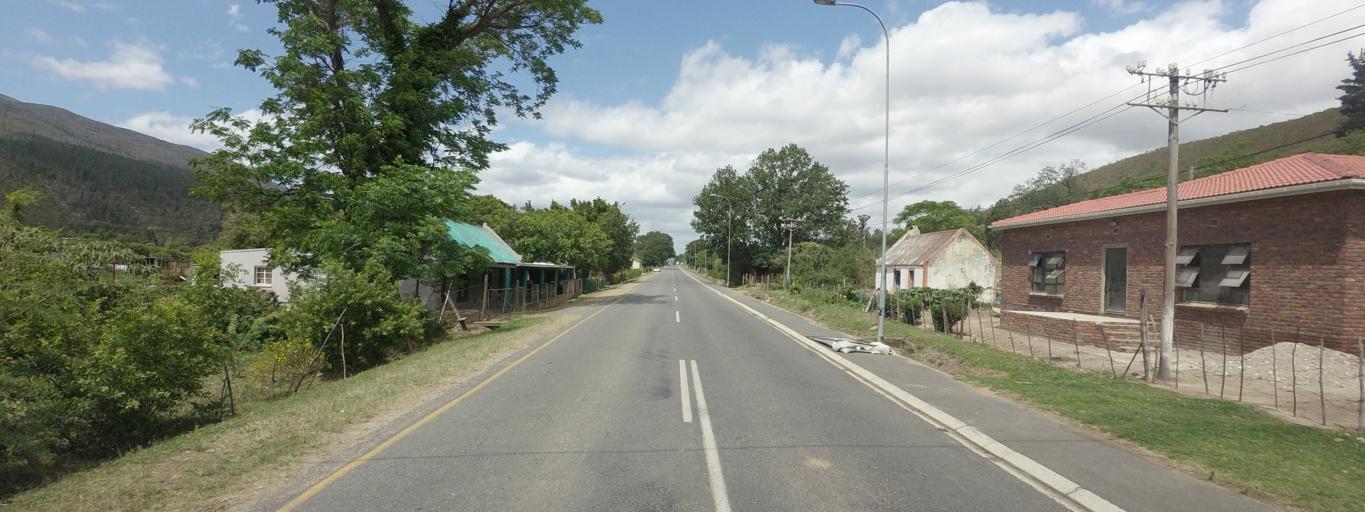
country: ZA
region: Western Cape
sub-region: Overberg District Municipality
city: Swellendam
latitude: -34.0034
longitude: 20.6429
